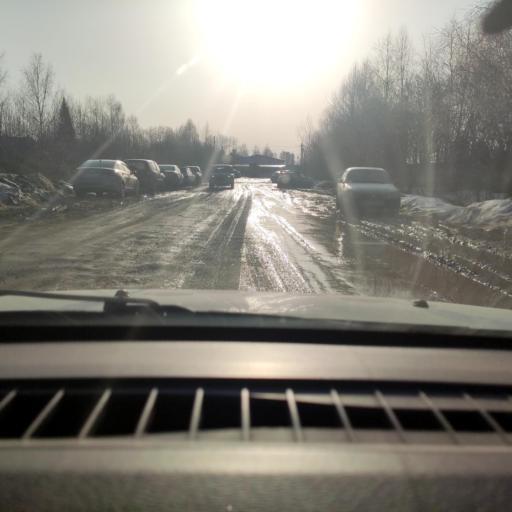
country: RU
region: Perm
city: Polazna
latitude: 58.1765
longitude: 56.4090
